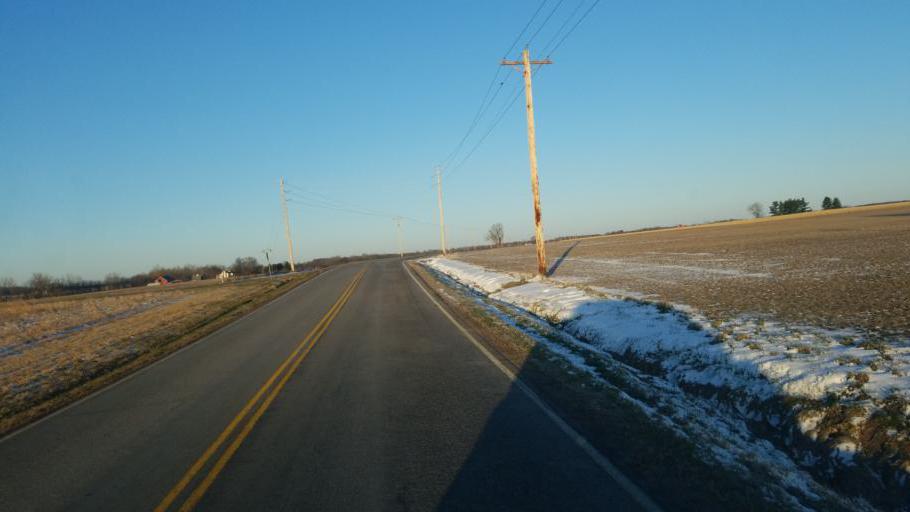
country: US
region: Ohio
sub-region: Highland County
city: Leesburg
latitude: 39.2625
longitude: -83.5166
